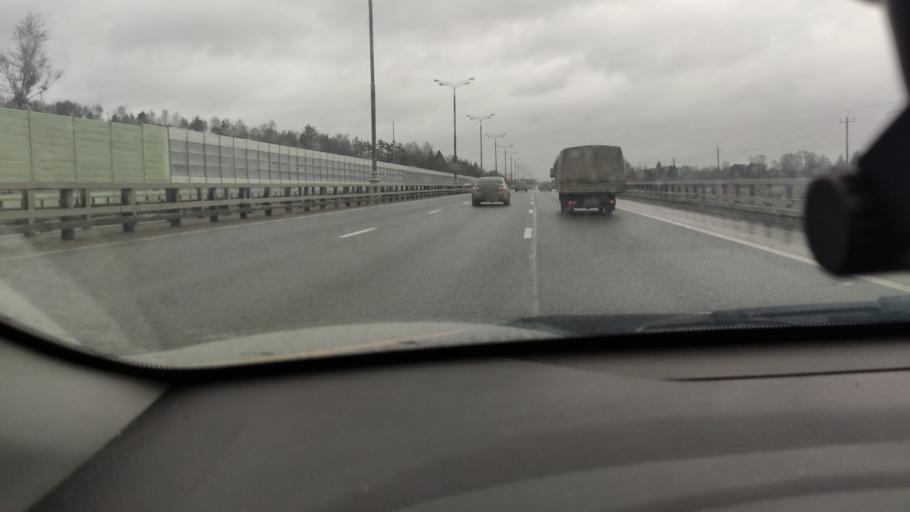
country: RU
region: Moskovskaya
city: Aprelevka
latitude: 55.5291
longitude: 37.0382
